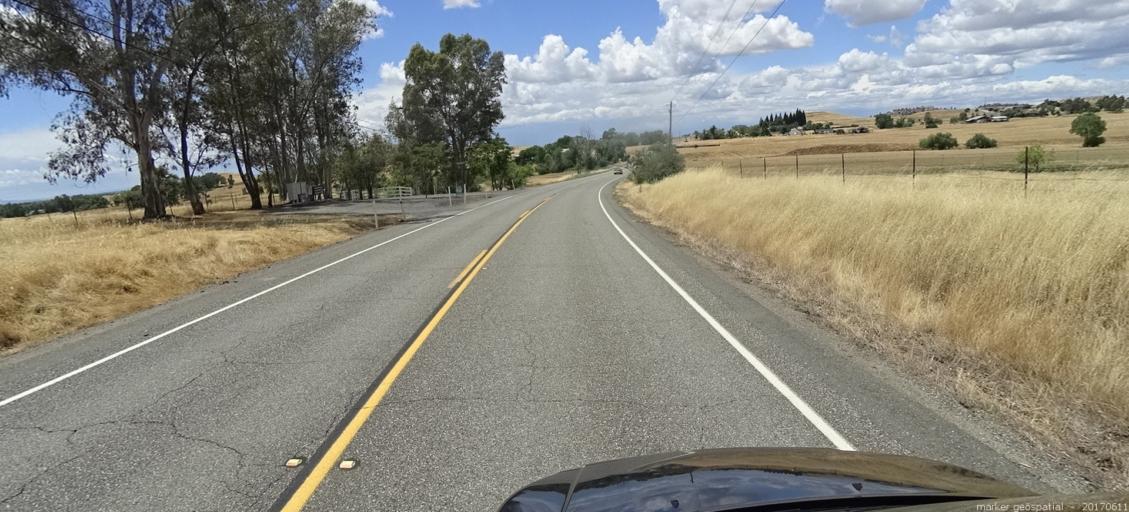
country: US
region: California
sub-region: Butte County
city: Paradise
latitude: 39.6475
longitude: -121.6075
